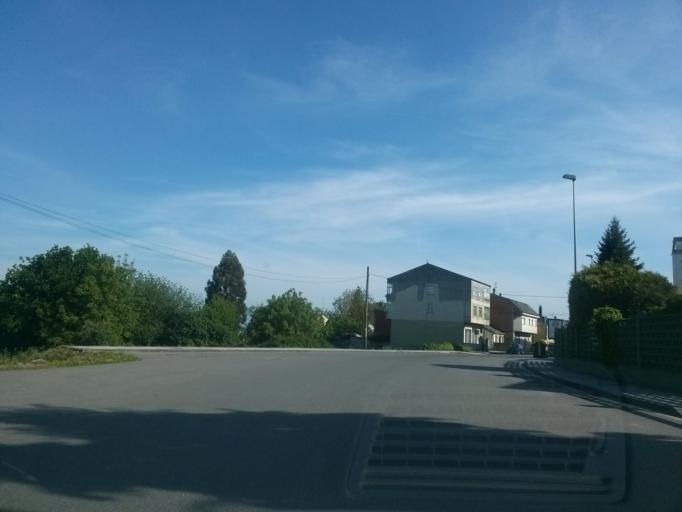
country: ES
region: Galicia
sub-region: Provincia de Lugo
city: Lugo
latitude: 43.0307
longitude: -7.5636
